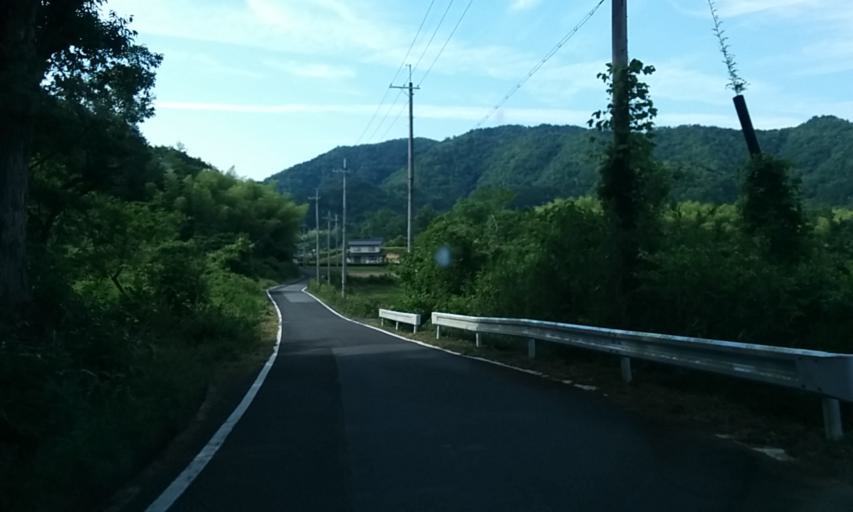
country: JP
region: Kyoto
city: Ayabe
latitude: 35.3588
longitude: 135.2067
